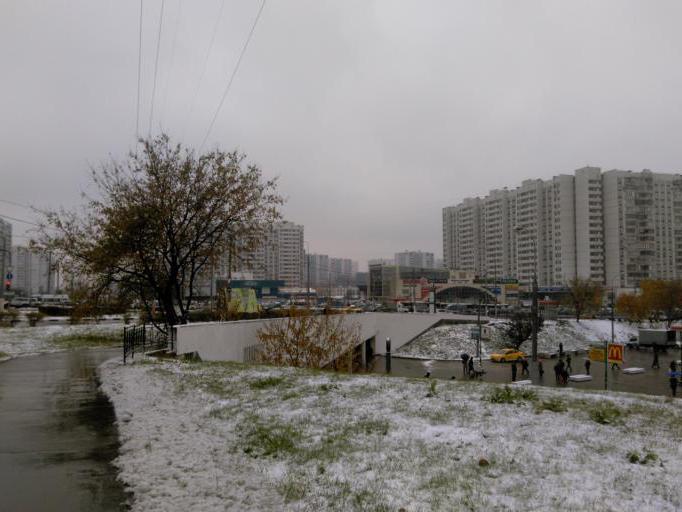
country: RU
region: Moscow
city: Nagornyy
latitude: 55.6412
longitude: 37.6040
